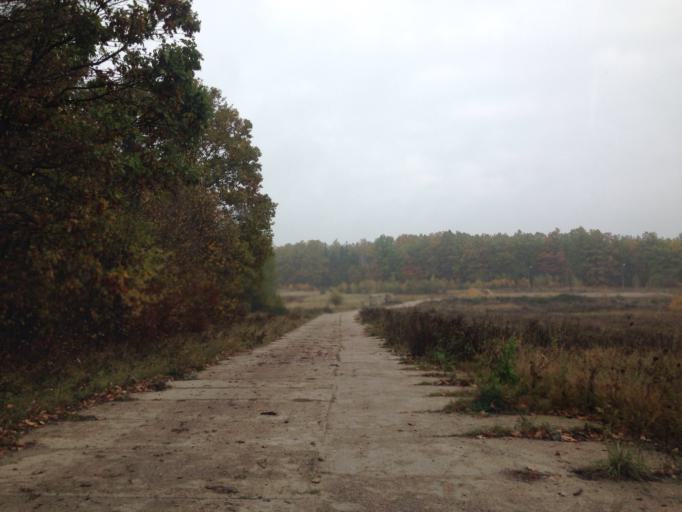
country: PL
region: Warmian-Masurian Voivodeship
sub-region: Powiat dzialdowski
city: Lidzbark
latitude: 53.2393
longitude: 19.7468
